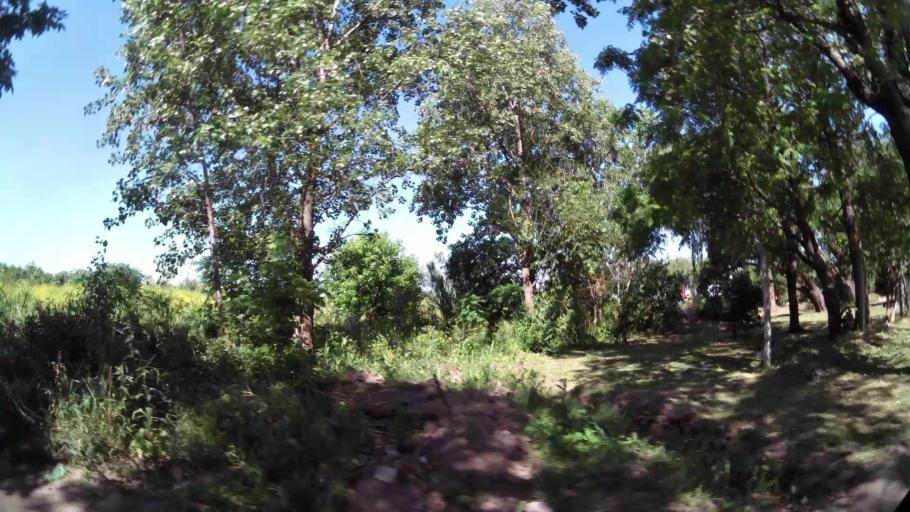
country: AR
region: Buenos Aires F.D.
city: Villa Lugano
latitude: -34.7021
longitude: -58.4702
